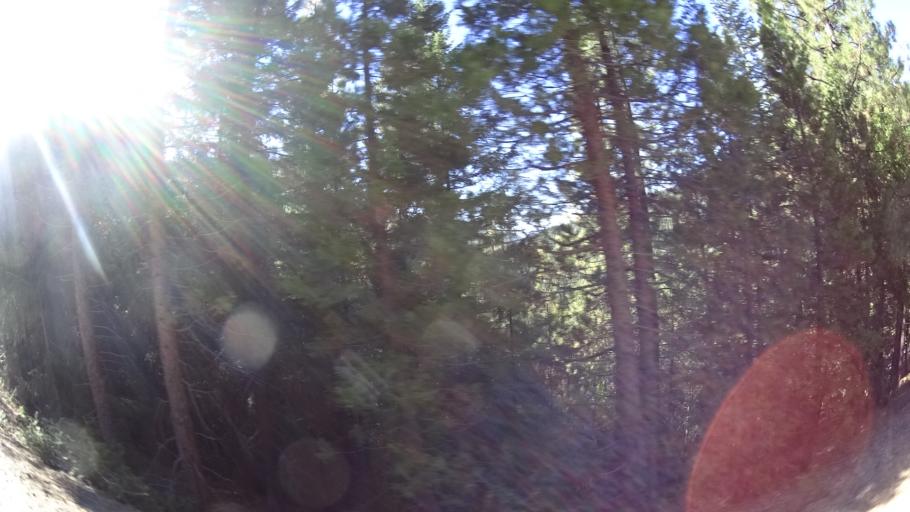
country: US
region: California
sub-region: Trinity County
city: Weaverville
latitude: 41.2231
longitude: -123.0136
